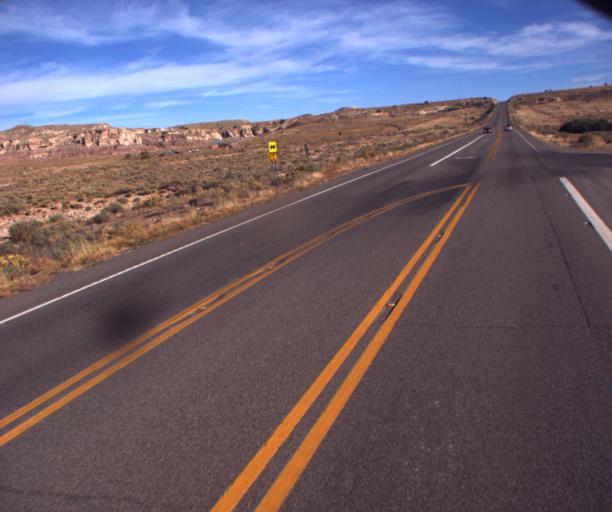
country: US
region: New Mexico
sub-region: San Juan County
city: Shiprock
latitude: 36.9302
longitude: -109.1041
